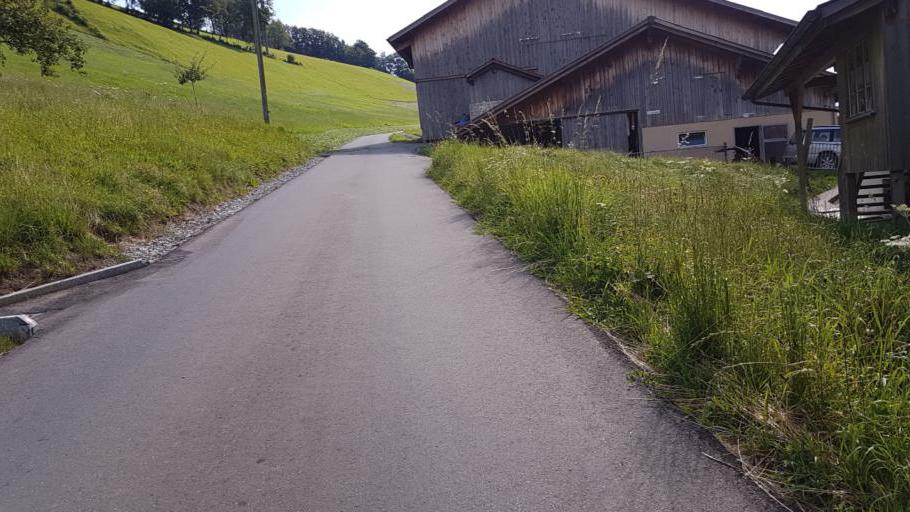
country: CH
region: Bern
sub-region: Obersimmental-Saanen District
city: Boltigen
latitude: 46.6625
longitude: 7.4574
